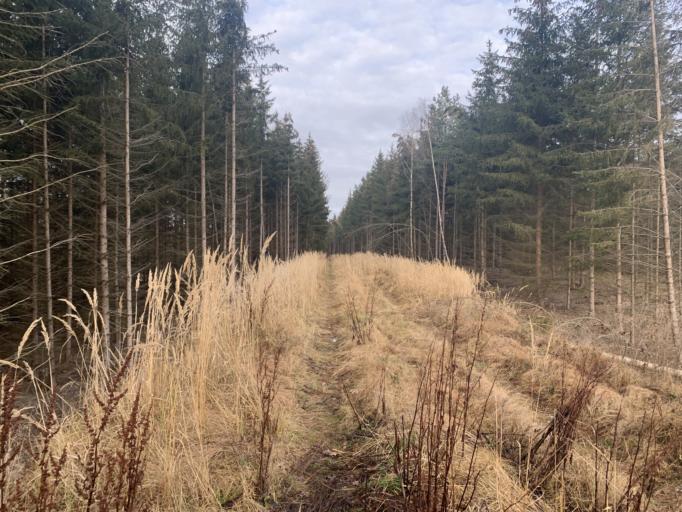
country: CZ
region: Plzensky
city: Zbiroh
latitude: 49.8247
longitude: 13.7936
